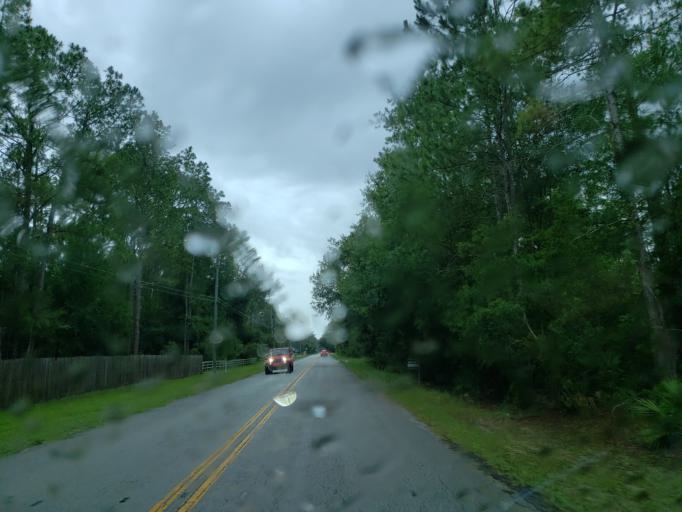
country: US
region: Florida
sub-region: Pasco County
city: Wesley Chapel
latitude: 28.2675
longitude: -82.3531
